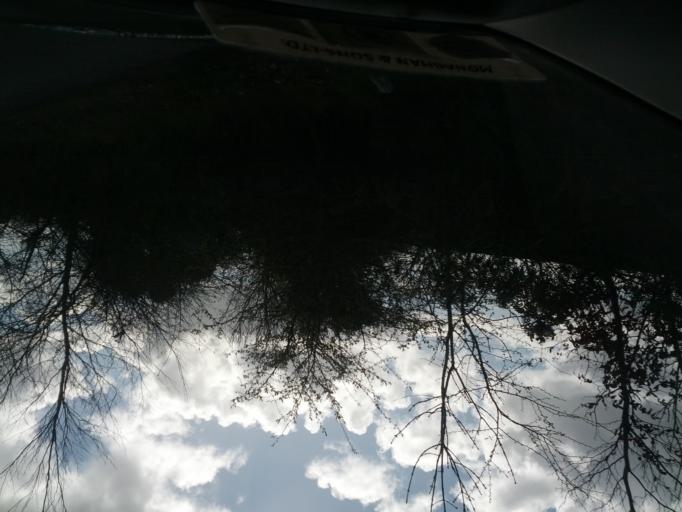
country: IE
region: Connaught
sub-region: County Galway
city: Claregalway
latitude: 53.2963
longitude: -8.9728
